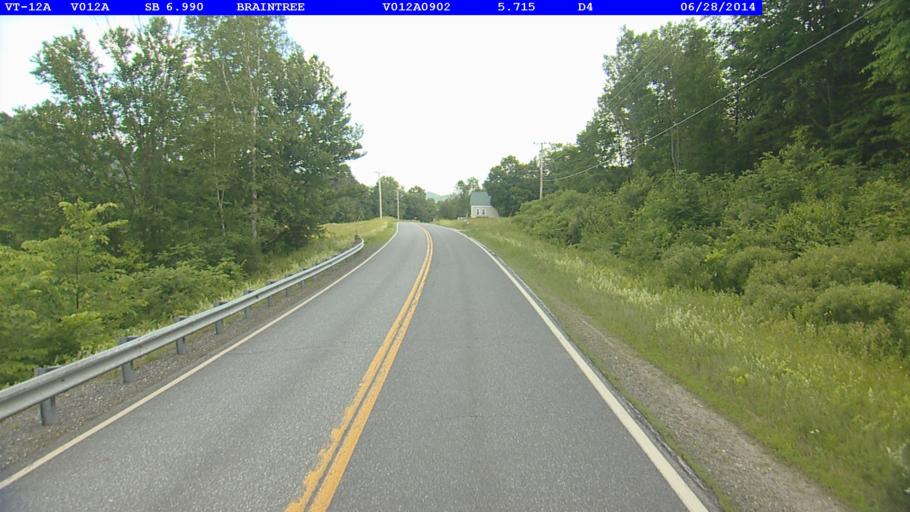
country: US
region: Vermont
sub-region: Orange County
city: Randolph
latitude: 43.9896
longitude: -72.7529
